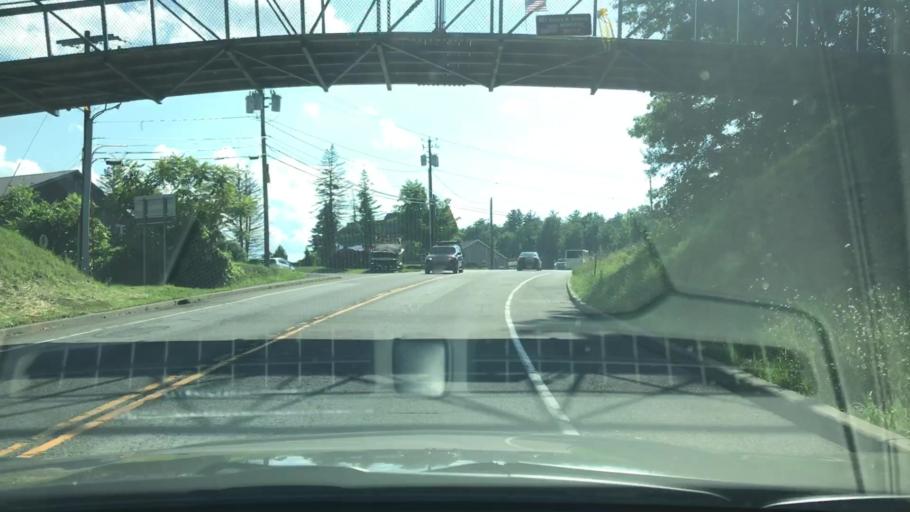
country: US
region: New York
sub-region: Warren County
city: Glens Falls North
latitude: 43.3697
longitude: -73.6957
